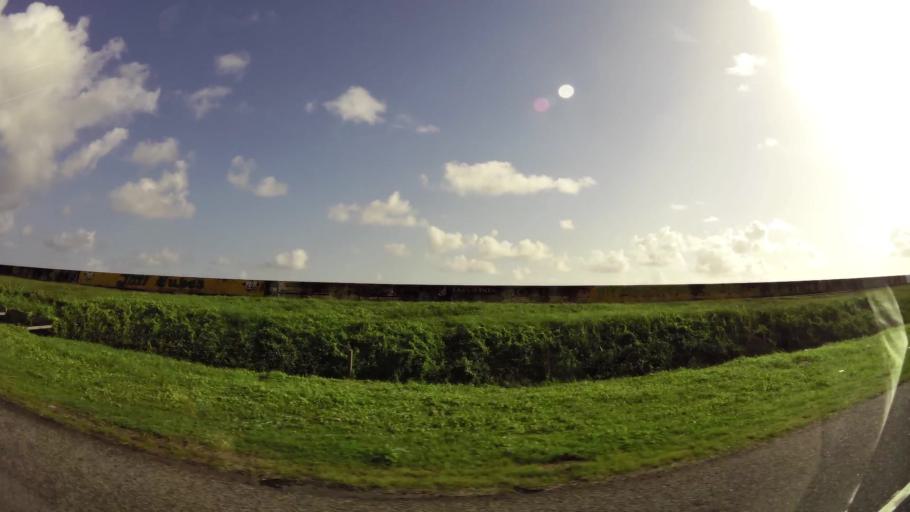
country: GY
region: Demerara-Mahaica
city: Georgetown
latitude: 6.8255
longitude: -58.1154
